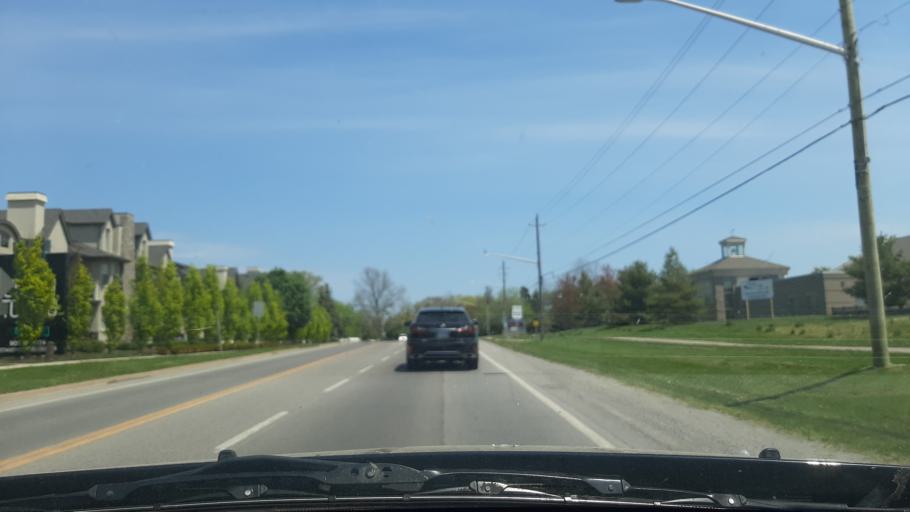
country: US
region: New York
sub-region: Niagara County
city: Youngstown
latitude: 43.2484
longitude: -79.0885
